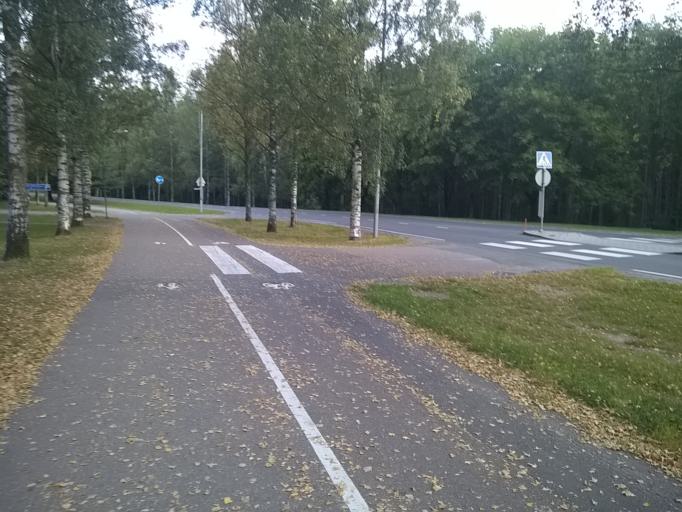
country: FI
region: Pirkanmaa
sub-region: Tampere
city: Tampere
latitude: 61.4483
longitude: 23.8344
